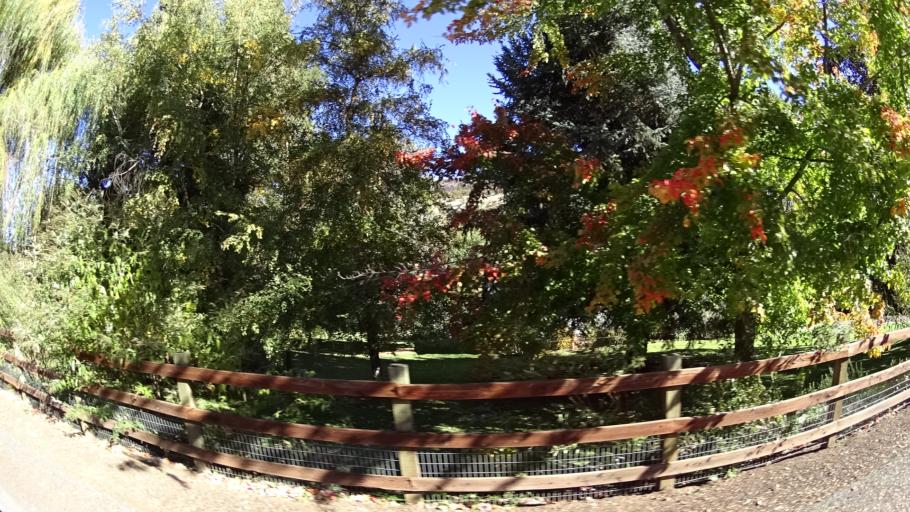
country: US
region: California
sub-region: Siskiyou County
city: Montague
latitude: 41.9661
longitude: -122.2737
